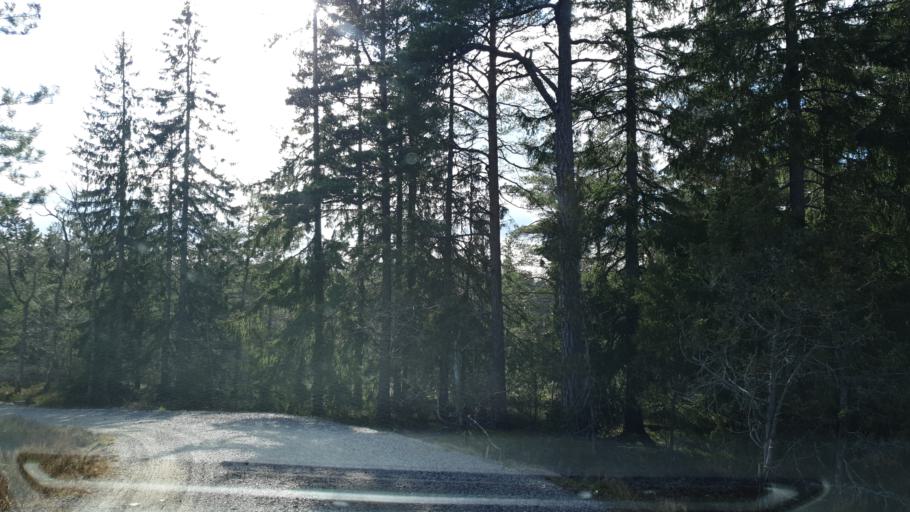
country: SE
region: Stockholm
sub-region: Varmdo Kommun
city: Holo
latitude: 59.2896
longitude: 18.6598
